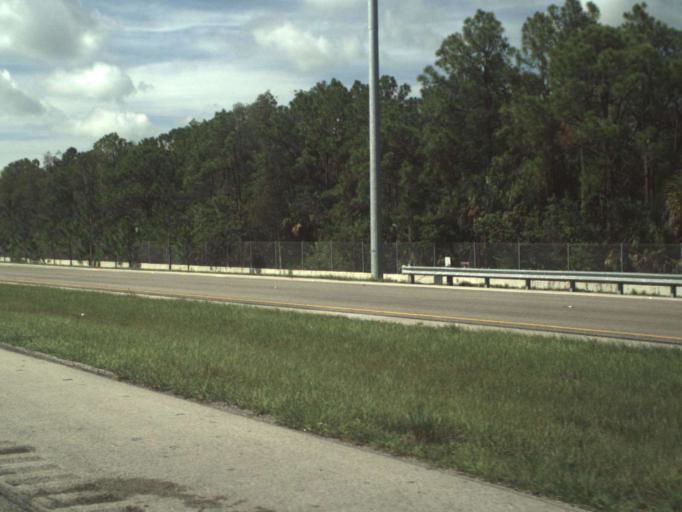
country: US
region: Florida
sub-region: Palm Beach County
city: Palm Beach Gardens
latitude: 26.8783
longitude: -80.1259
